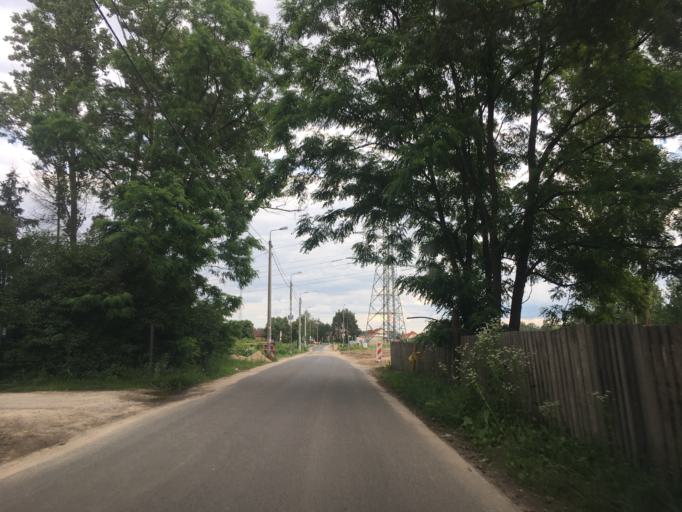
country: PL
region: Masovian Voivodeship
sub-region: Powiat piaseczynski
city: Lesznowola
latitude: 52.0753
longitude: 20.9605
